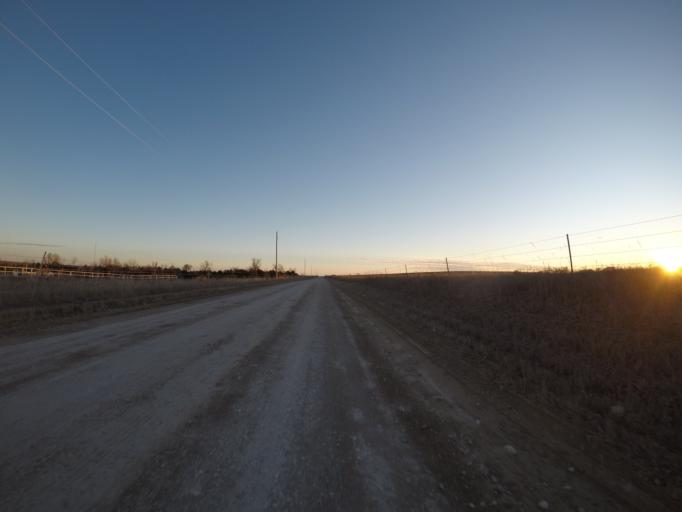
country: US
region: Kansas
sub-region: Riley County
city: Manhattan
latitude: 39.2736
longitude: -96.4827
